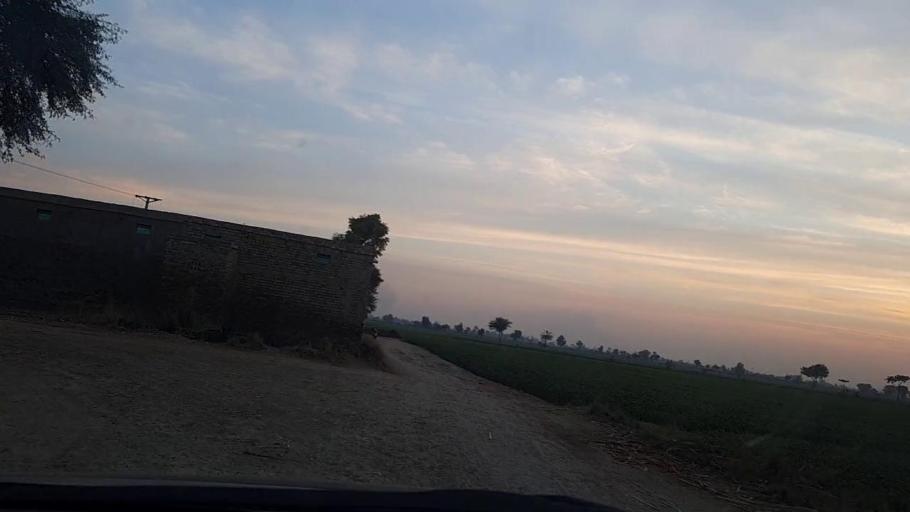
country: PK
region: Sindh
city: Sakrand
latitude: 26.2014
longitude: 68.3183
